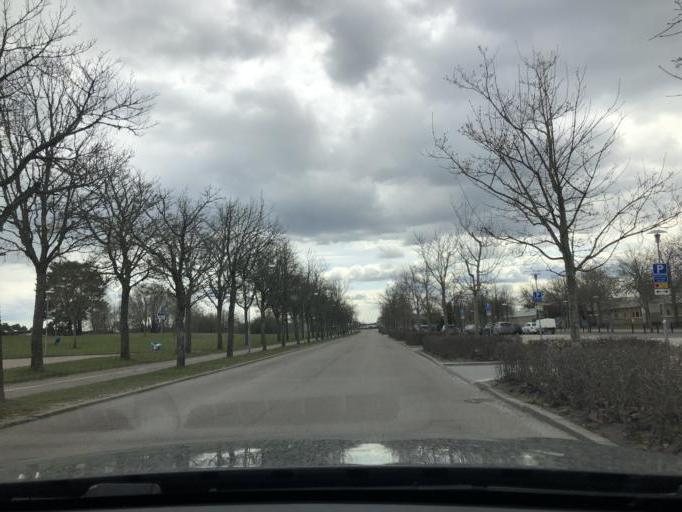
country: SE
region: Uppsala
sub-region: Uppsala Kommun
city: Uppsala
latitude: 59.8216
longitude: 17.6563
